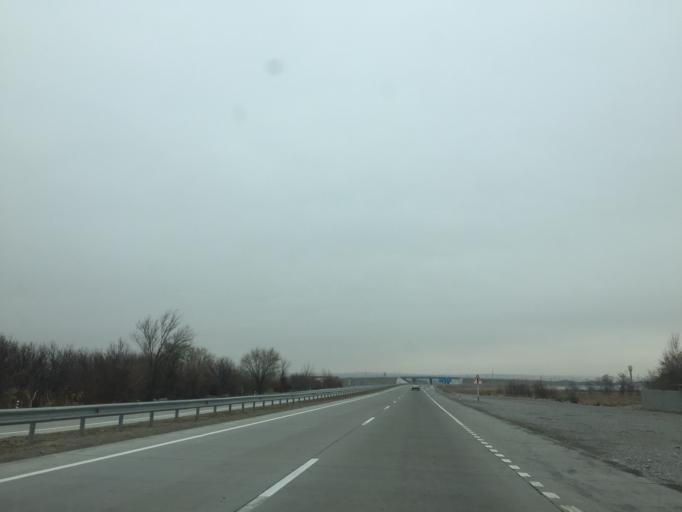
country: KZ
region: Ongtustik Qazaqstan
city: Aksu
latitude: 42.4717
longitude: 69.8073
